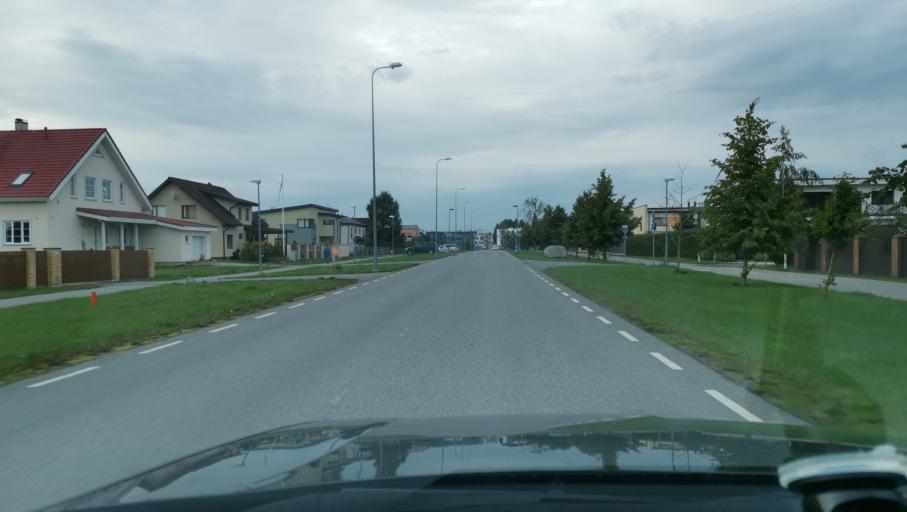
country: EE
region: Harju
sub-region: Saue vald
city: Laagri
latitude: 59.4251
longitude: 24.6225
